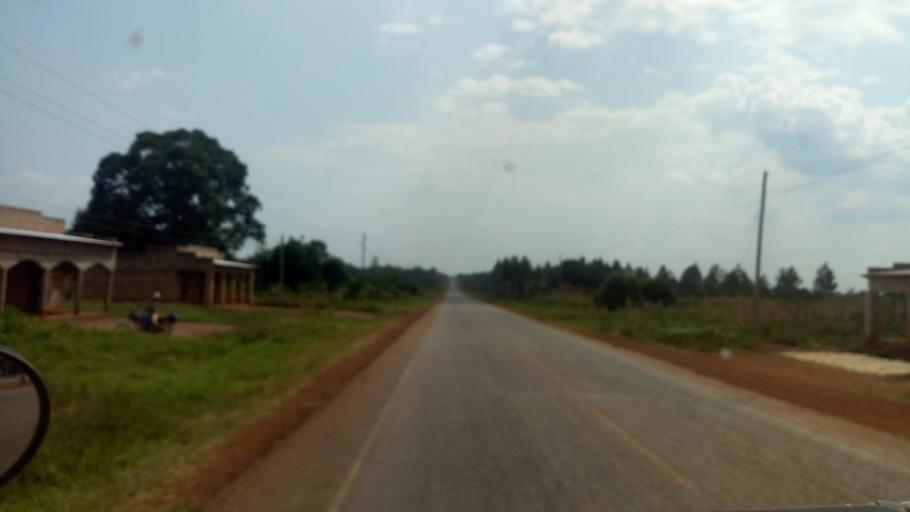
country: UG
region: Northern Region
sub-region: Oyam District
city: Oyam
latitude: 2.2183
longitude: 32.3990
